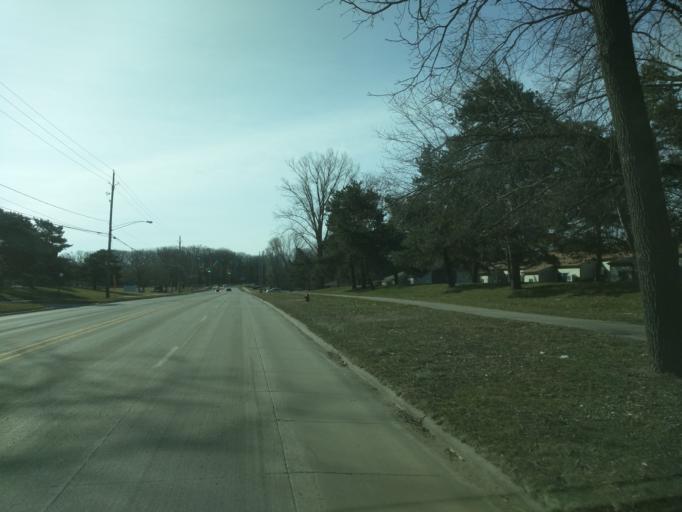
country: US
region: Michigan
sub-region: Ingham County
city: Haslett
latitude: 42.7583
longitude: -84.4106
